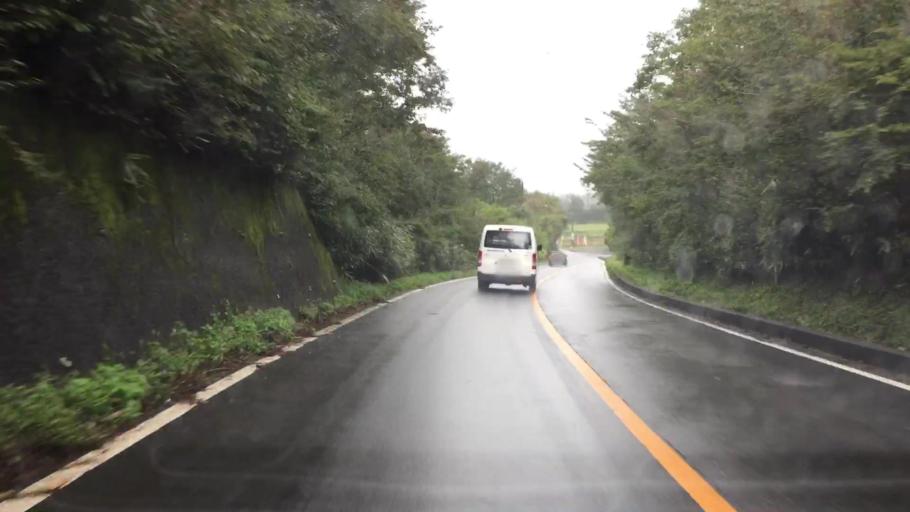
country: JP
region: Yamanashi
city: Fujikawaguchiko
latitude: 35.4218
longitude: 138.6245
